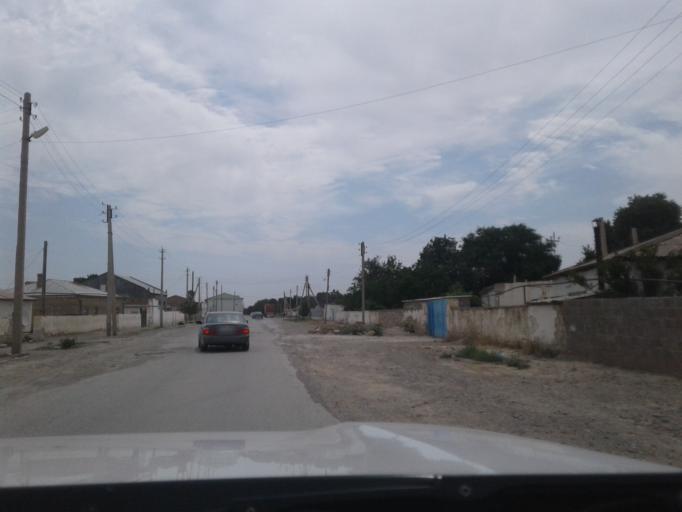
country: TM
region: Balkan
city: Serdar
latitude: 38.9884
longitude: 56.2793
